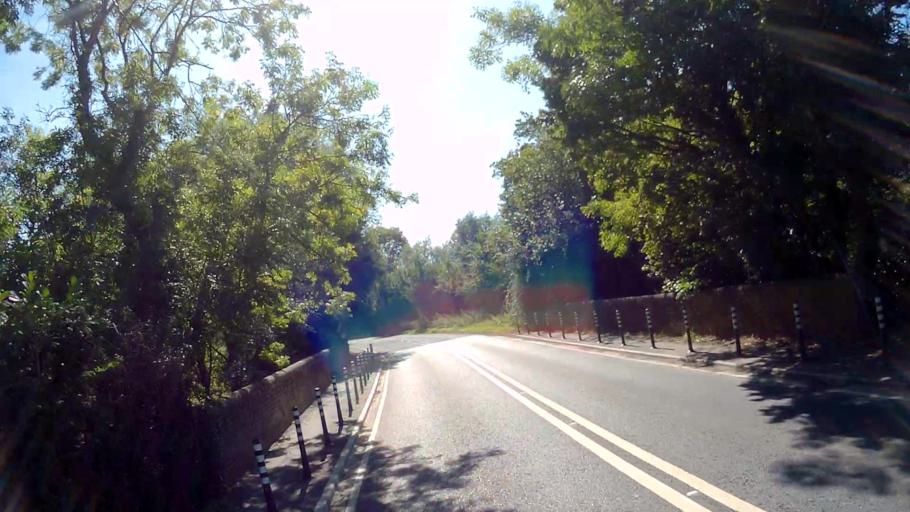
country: GB
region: England
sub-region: Wokingham
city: Swallowfield
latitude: 51.3823
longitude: -0.9658
